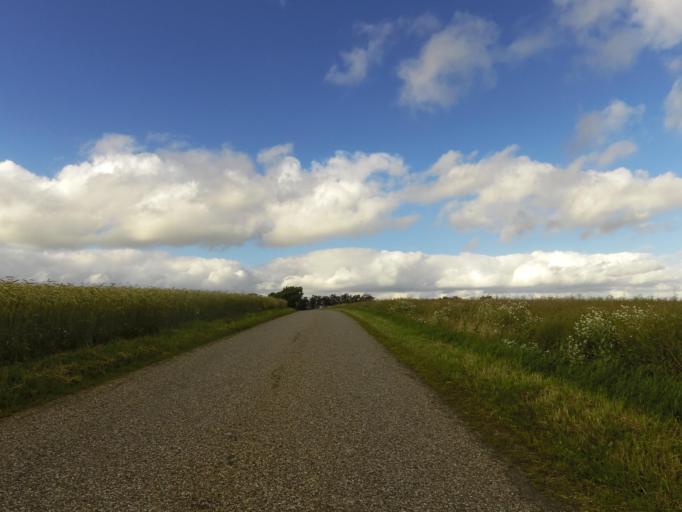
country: DK
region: South Denmark
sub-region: Tonder Kommune
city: Toftlund
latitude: 55.1421
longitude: 9.0819
